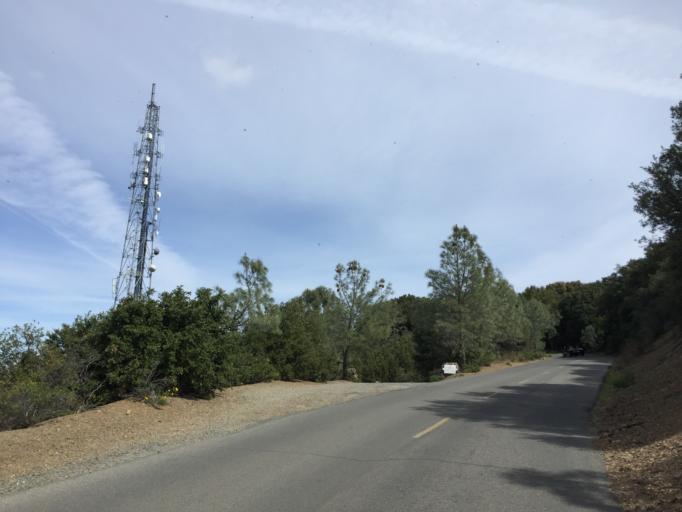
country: US
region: California
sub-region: Contra Costa County
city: Diablo
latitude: 37.8809
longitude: -121.9205
